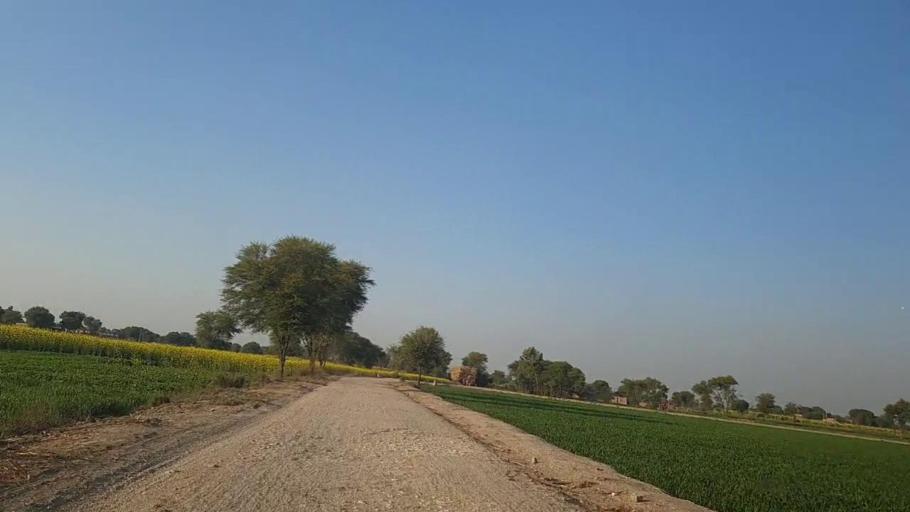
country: PK
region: Sindh
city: Sakrand
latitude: 26.3021
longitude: 68.1267
